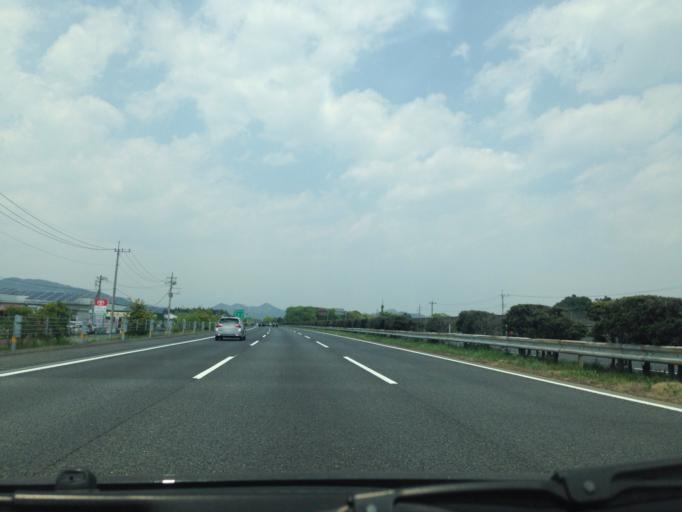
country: JP
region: Tochigi
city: Utsunomiya-shi
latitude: 36.6088
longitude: 139.8441
